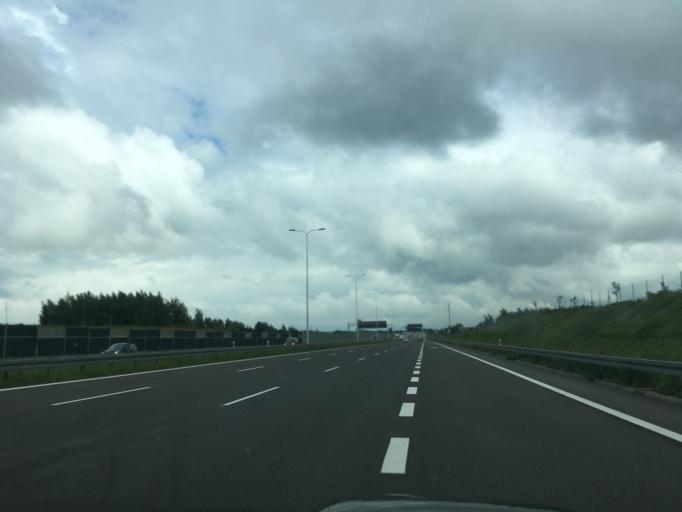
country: PL
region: Lublin Voivodeship
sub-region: Powiat lubelski
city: Jastkow
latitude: 51.2902
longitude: 22.4641
